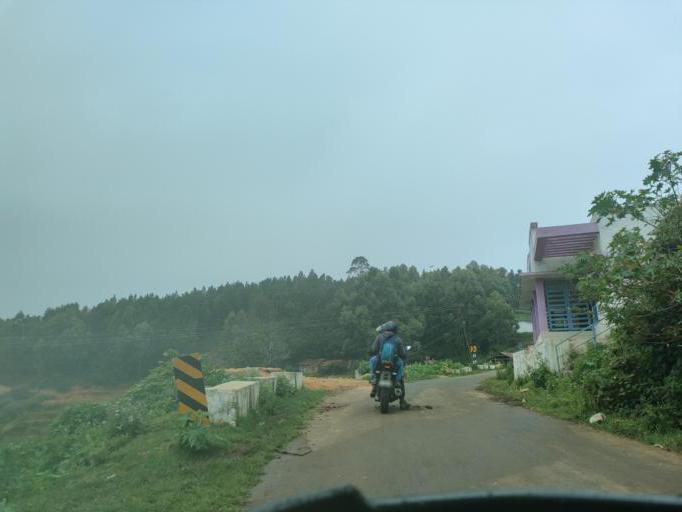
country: IN
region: Tamil Nadu
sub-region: Dindigul
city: Kodaikanal
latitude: 10.2230
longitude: 77.3459
